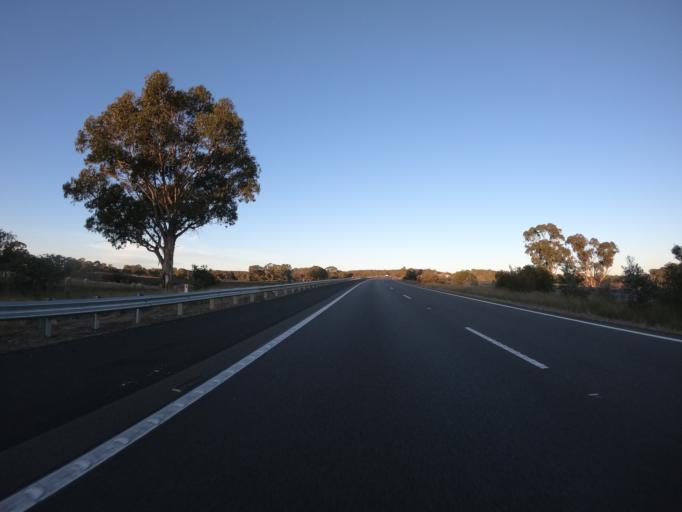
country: AU
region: New South Wales
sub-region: Goulburn Mulwaree
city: Goulburn
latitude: -34.7850
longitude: 149.6597
